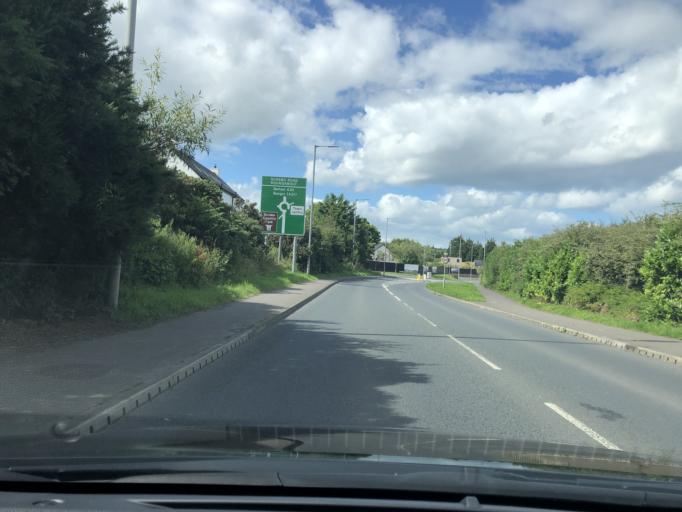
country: GB
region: Northern Ireland
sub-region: Ards District
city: Newtownards
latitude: 54.5873
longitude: -5.7125
